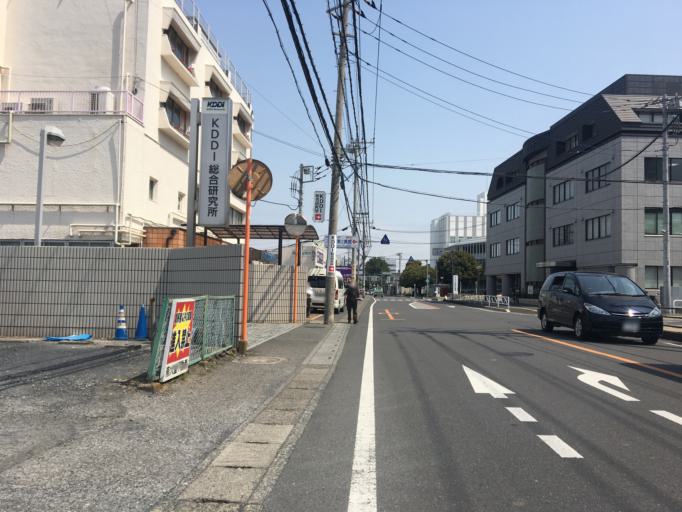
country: JP
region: Saitama
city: Kamifukuoka
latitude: 35.8787
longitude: 139.5185
